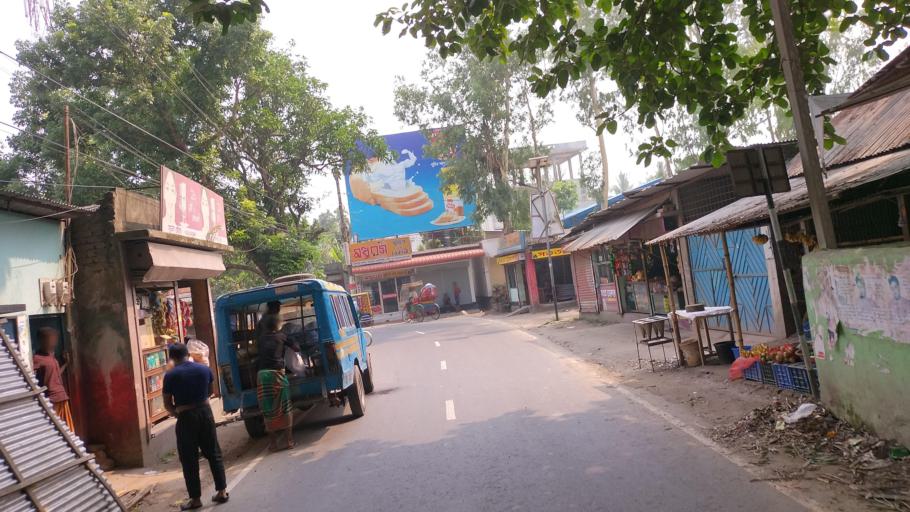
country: BD
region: Dhaka
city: Azimpur
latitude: 23.6980
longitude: 90.2941
